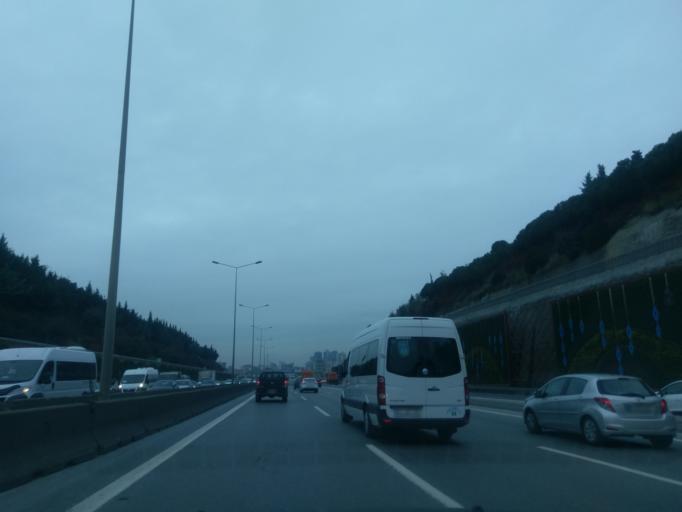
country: TR
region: Istanbul
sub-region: Atasehir
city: Atasehir
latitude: 40.9564
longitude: 29.1142
